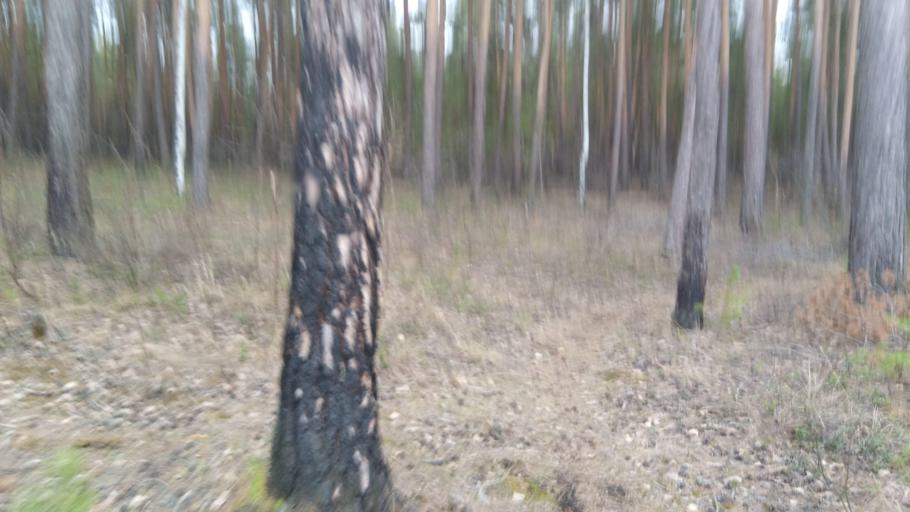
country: RU
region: Chelyabinsk
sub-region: Gorod Chelyabinsk
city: Chelyabinsk
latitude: 55.1352
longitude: 61.3395
